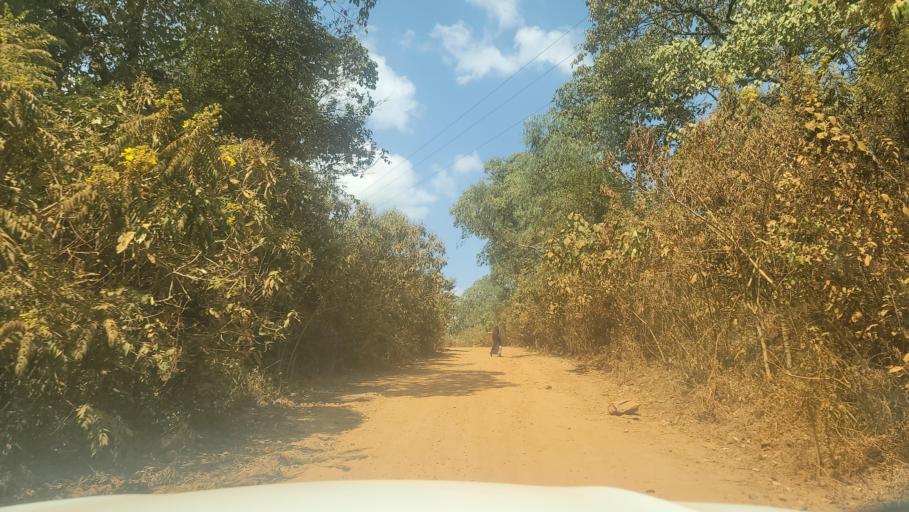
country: ET
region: Oromiya
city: Agaro
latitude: 7.8384
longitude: 36.5409
